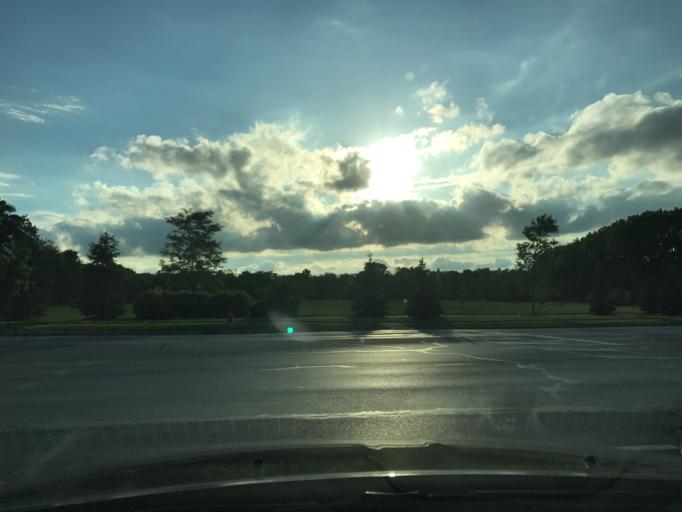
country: US
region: Illinois
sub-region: DuPage County
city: Naperville
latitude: 41.7579
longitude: -88.1578
